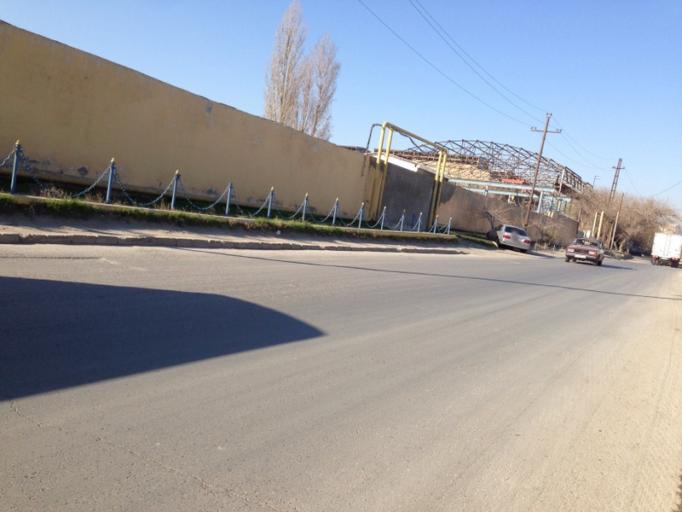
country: AZ
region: Baki
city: Baku
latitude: 40.4213
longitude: 49.8643
